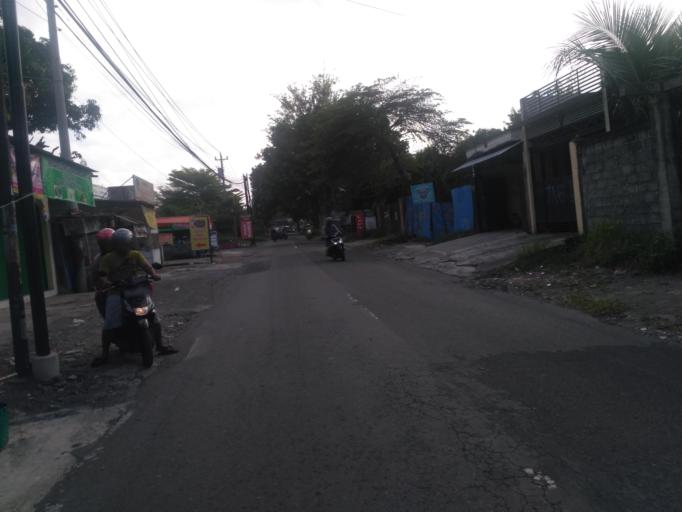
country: ID
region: Daerah Istimewa Yogyakarta
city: Yogyakarta
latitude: -7.7655
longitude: 110.3444
